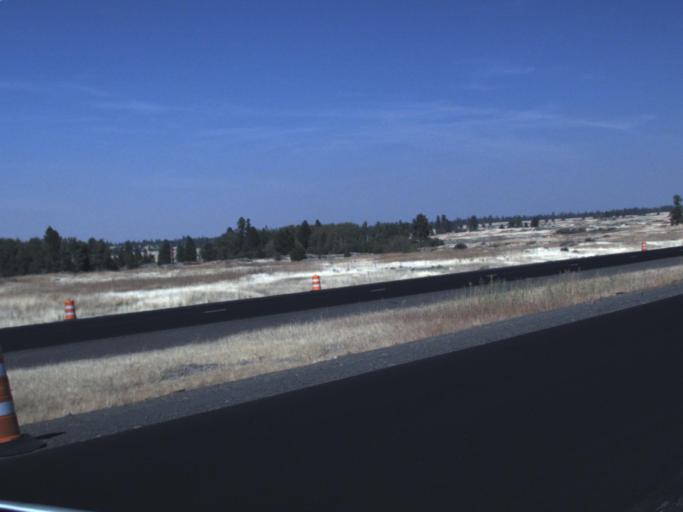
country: US
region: Washington
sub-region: Spokane County
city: Medical Lake
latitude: 47.3875
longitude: -117.8541
